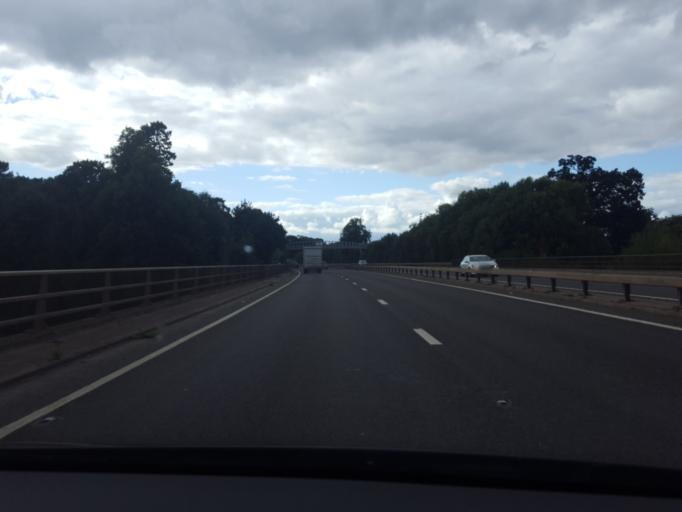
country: GB
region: England
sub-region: Leicestershire
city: Barrow upon Soar
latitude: 52.7480
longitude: -1.1581
